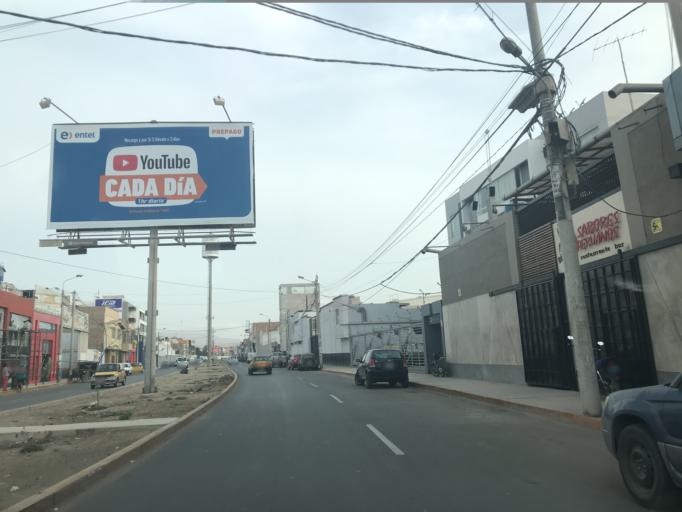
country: PE
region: Lambayeque
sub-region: Provincia de Chiclayo
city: Chiclayo
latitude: -6.7886
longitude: -79.8441
